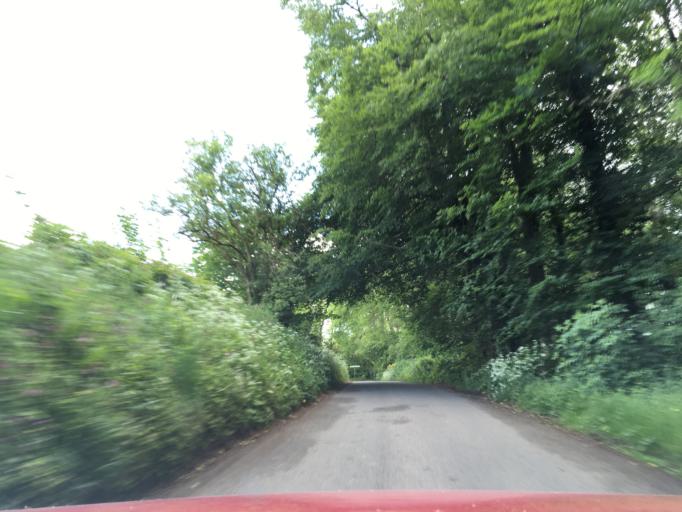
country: GB
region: England
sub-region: Gloucestershire
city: Shurdington
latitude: 51.8067
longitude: -2.1138
